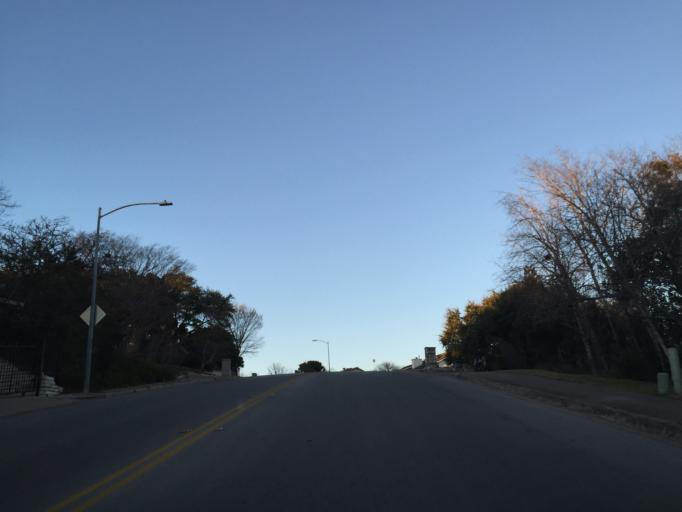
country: US
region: Texas
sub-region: Williamson County
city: Jollyville
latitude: 30.4041
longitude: -97.7594
